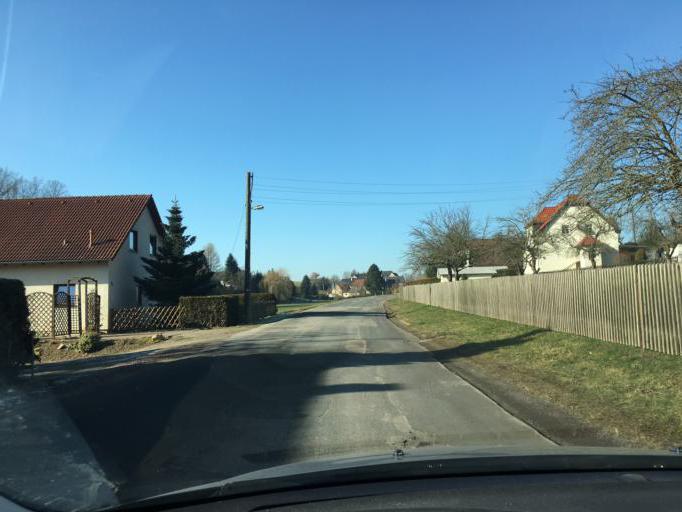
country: DE
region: Saxony
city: Penig
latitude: 50.9684
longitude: 12.7182
